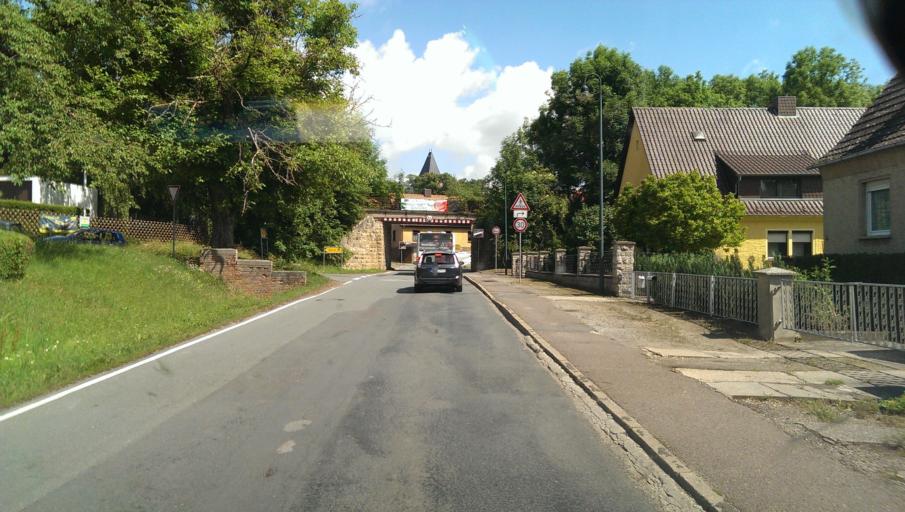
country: DE
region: Saxony-Anhalt
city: Bad Bibra
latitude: 51.2031
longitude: 11.5800
